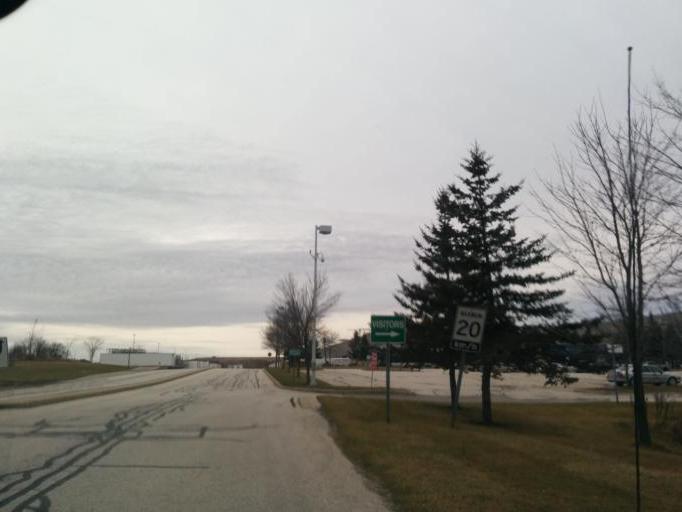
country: CA
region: Ontario
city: Shelburne
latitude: 44.0751
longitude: -80.1874
